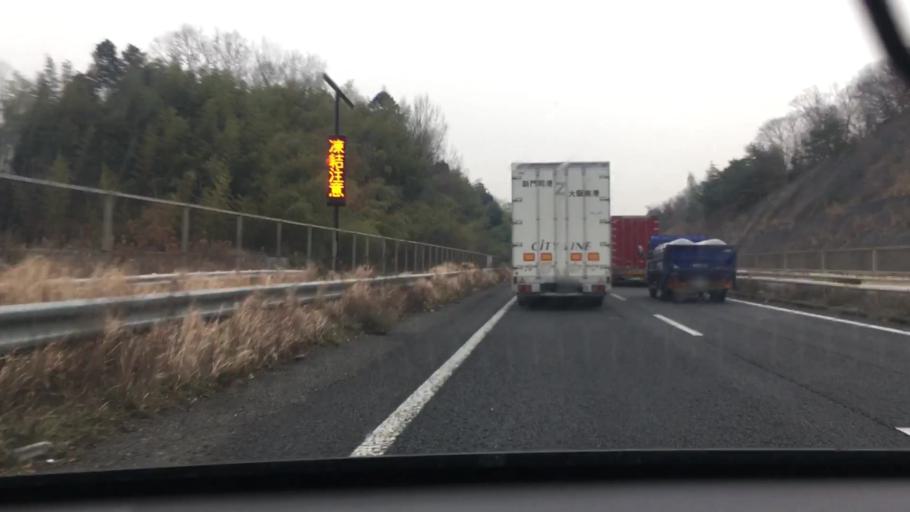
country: JP
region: Mie
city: Ueno-ebisumachi
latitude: 34.7851
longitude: 136.1596
